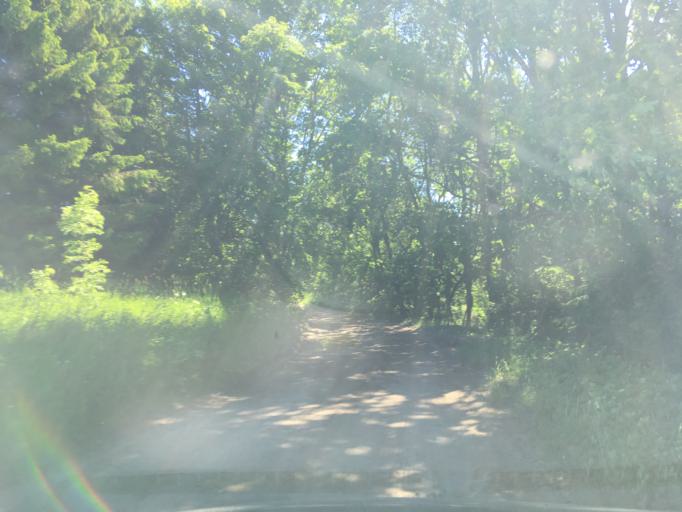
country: EE
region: Harju
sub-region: Rae vald
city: Vaida
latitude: 59.1580
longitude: 25.1296
